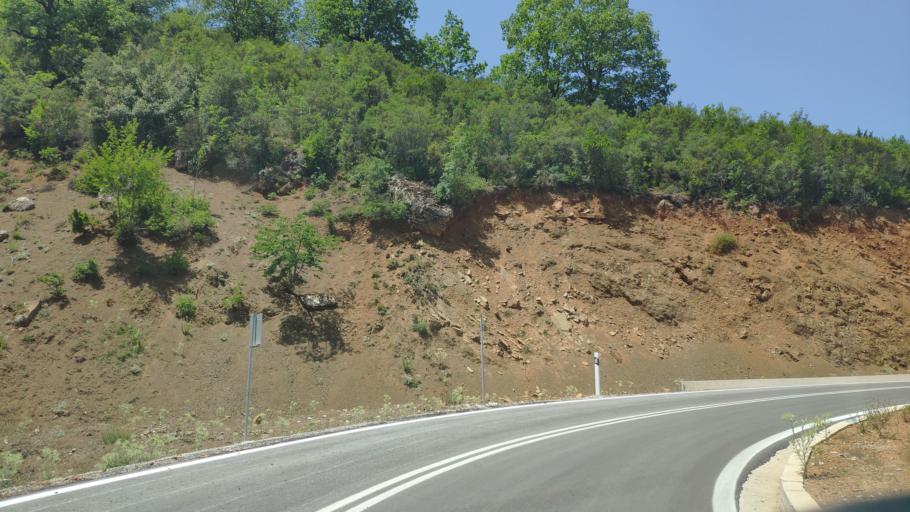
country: GR
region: Epirus
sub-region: Nomos Artas
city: Ano Kalentini
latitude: 39.1856
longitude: 21.3569
